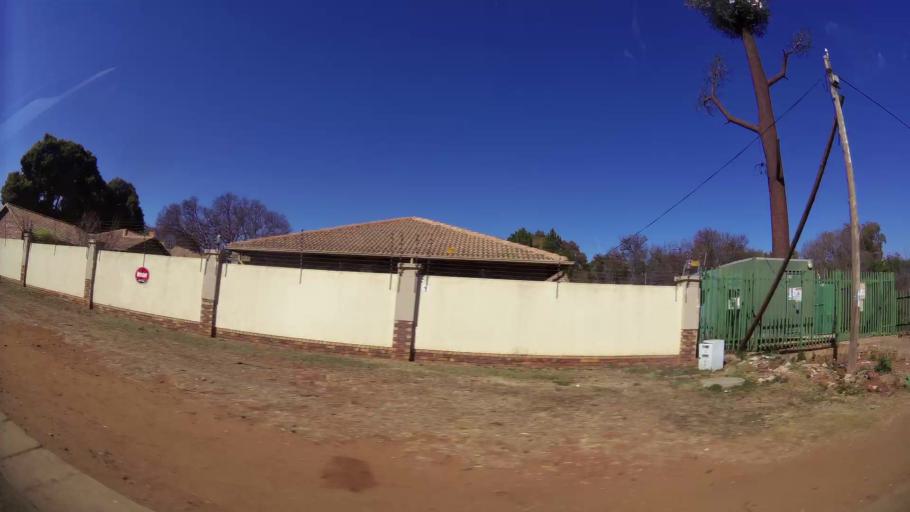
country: ZA
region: Gauteng
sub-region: City of Tshwane Metropolitan Municipality
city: Centurion
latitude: -25.8581
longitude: 28.1987
